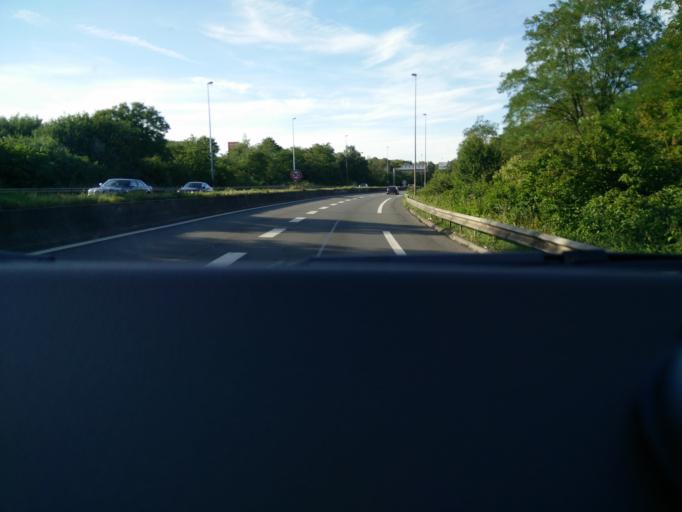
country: FR
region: Nord-Pas-de-Calais
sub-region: Departement du Nord
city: Lourches
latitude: 50.3050
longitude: 3.3718
